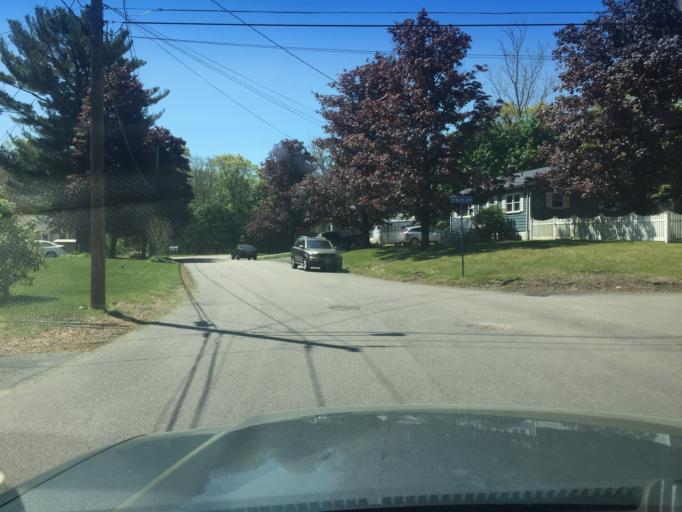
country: US
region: Massachusetts
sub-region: Norfolk County
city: Medway
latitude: 42.1555
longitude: -71.3992
